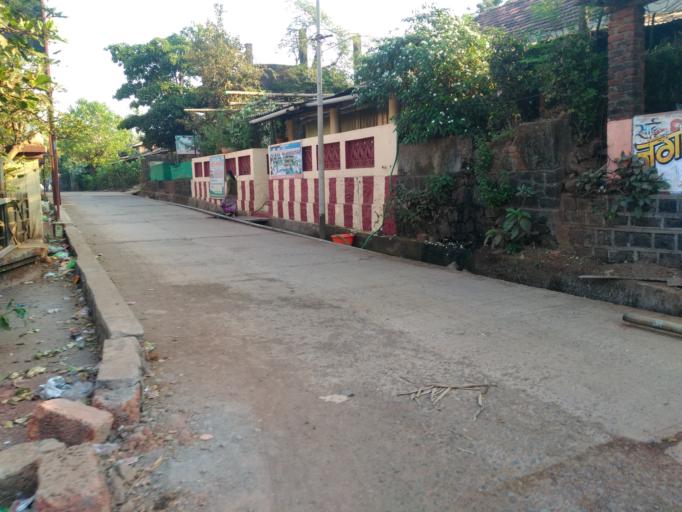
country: IN
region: Maharashtra
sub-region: Raigarh
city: Srivardhan
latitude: 17.9939
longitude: 73.0225
